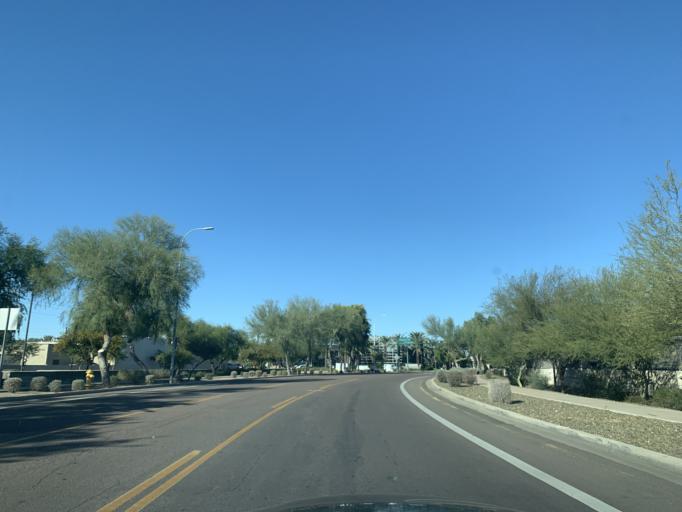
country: US
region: Arizona
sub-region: Maricopa County
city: Tempe Junction
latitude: 33.4206
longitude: -111.9811
